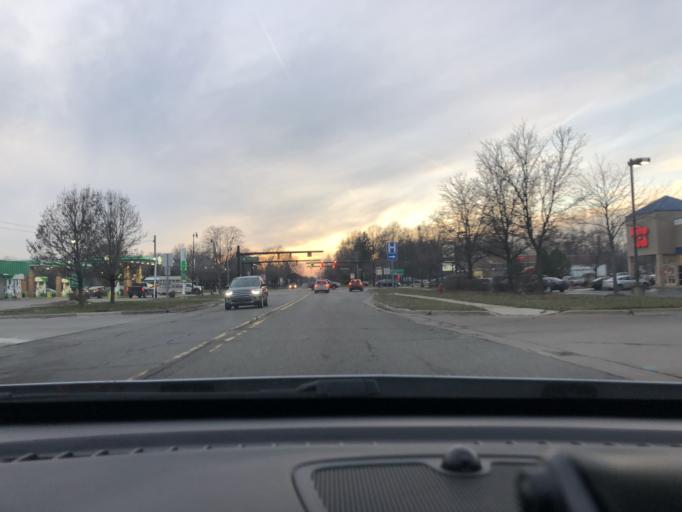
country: US
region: Michigan
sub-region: Wayne County
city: Taylor
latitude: 42.2411
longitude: -83.2682
